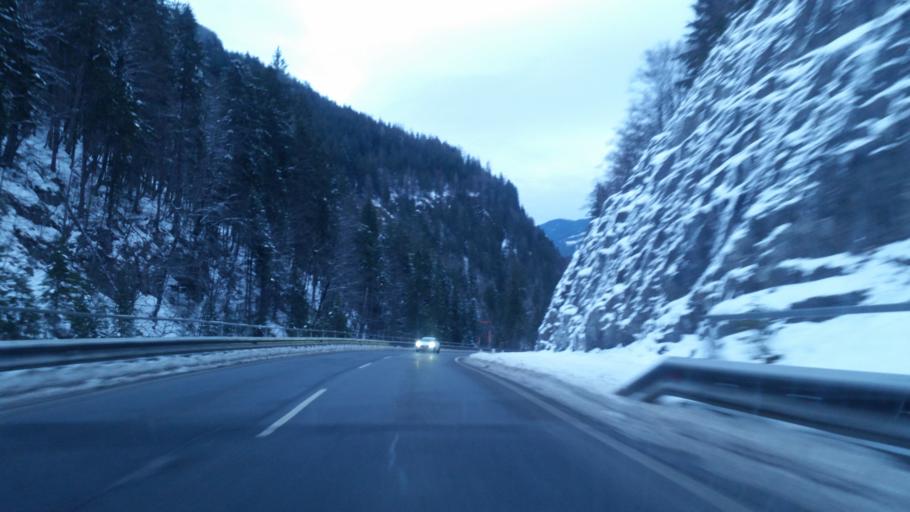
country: AT
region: Salzburg
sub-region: Politischer Bezirk Sankt Johann im Pongau
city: Untertauern
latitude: 47.2770
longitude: 13.5023
